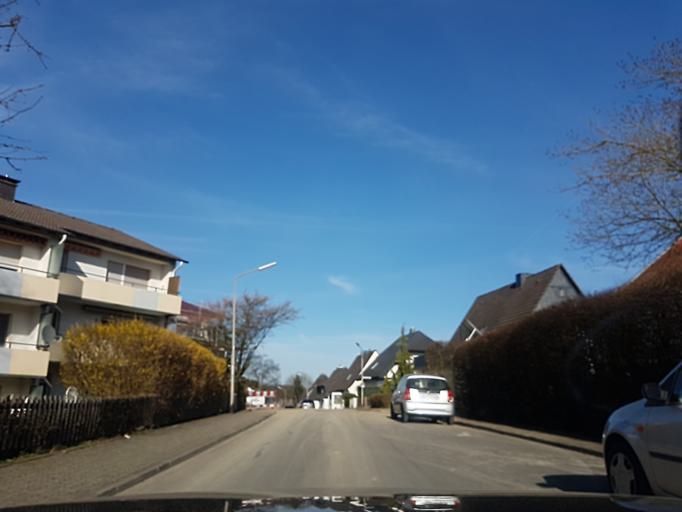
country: DE
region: North Rhine-Westphalia
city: Kierspe
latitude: 51.1309
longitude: 7.5999
